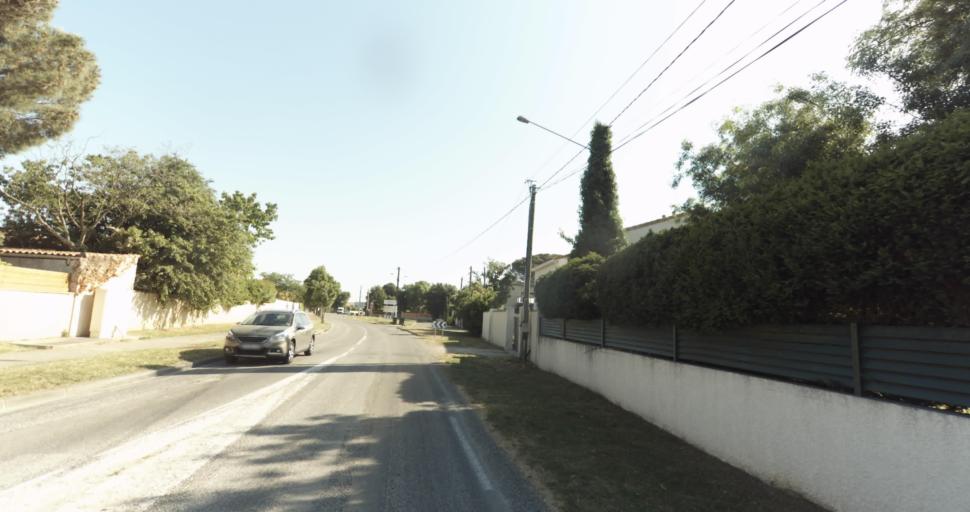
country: FR
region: Midi-Pyrenees
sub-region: Departement de la Haute-Garonne
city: Plaisance-du-Touch
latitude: 43.5538
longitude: 1.2954
